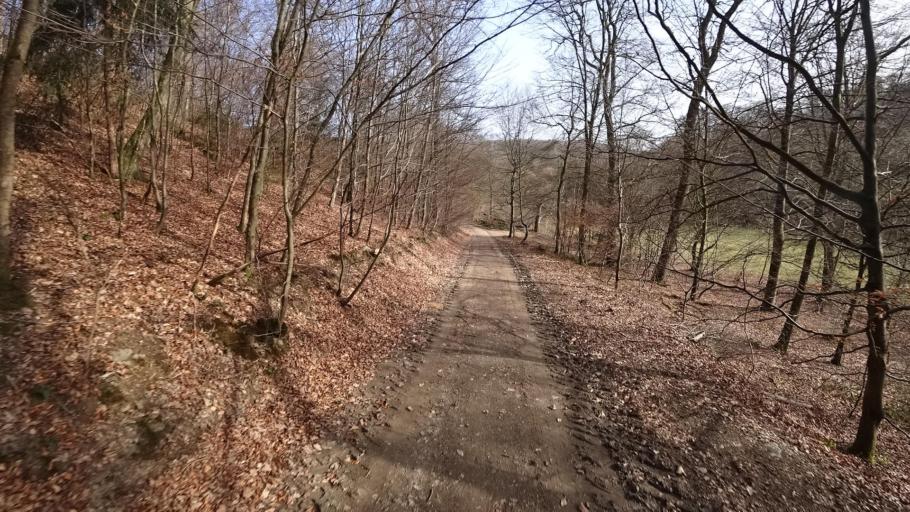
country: DE
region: Rheinland-Pfalz
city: Scheuerfeld
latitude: 50.7780
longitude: 7.8283
